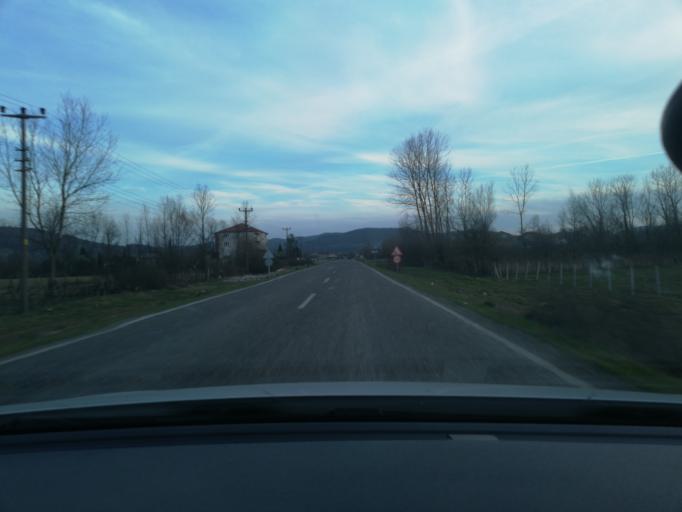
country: TR
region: Zonguldak
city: Saltukova
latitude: 41.5178
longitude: 32.1024
